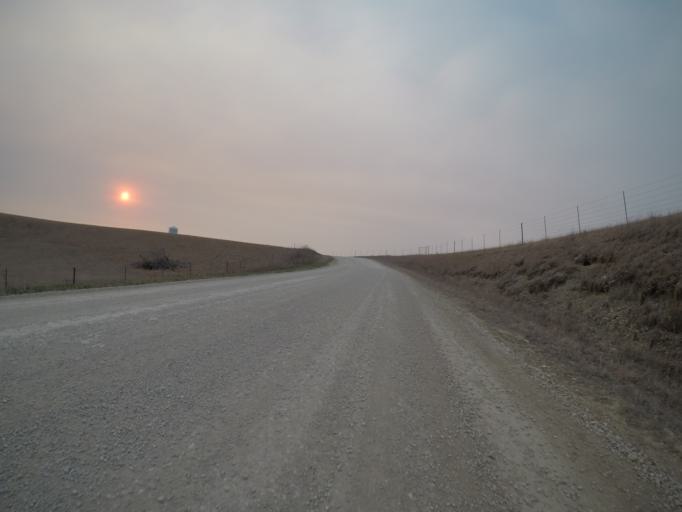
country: US
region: Kansas
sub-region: Riley County
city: Manhattan
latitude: 39.2290
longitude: -96.6409
